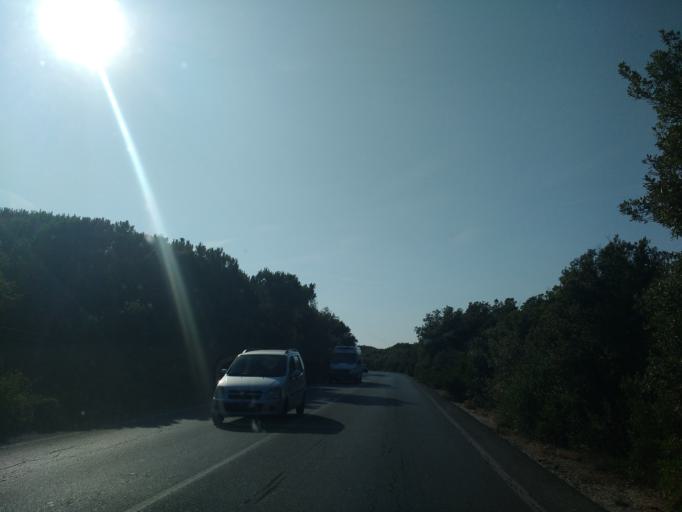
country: IT
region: Latium
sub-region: Citta metropolitana di Roma Capitale
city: Acilia-Castel Fusano-Ostia Antica
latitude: 41.6950
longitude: 12.3634
